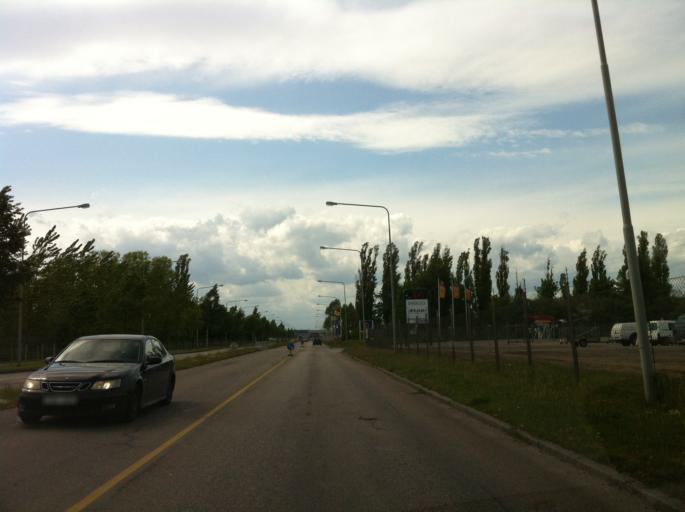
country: SE
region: Skane
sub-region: Landskrona
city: Landskrona
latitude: 55.8659
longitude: 12.8596
